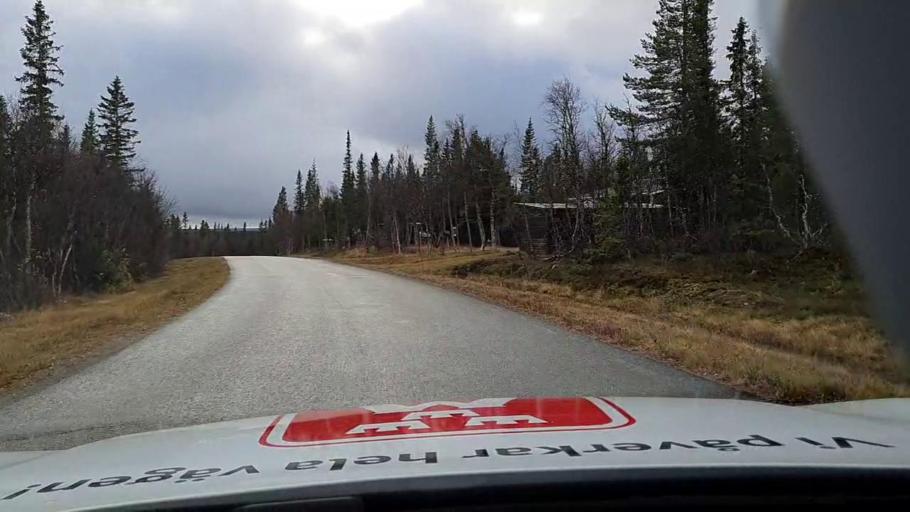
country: SE
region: Jaemtland
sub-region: Krokoms Kommun
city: Valla
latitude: 63.0262
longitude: 13.9443
